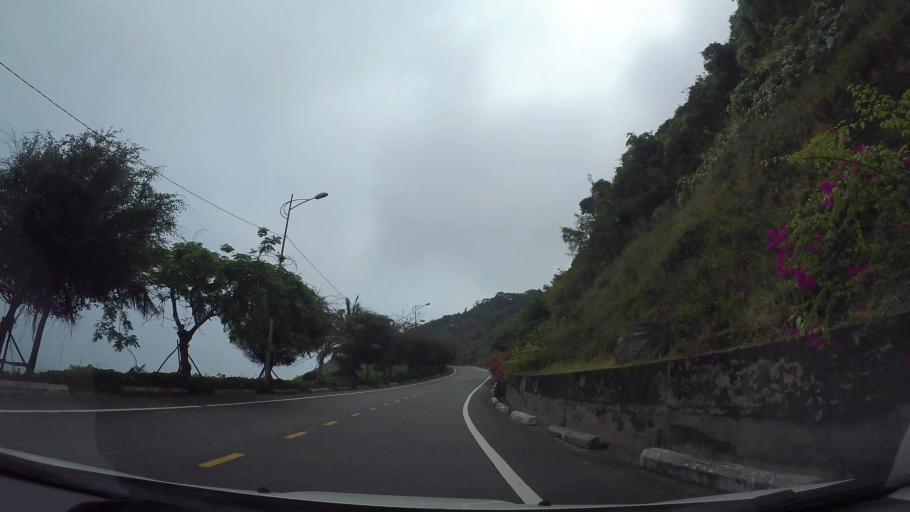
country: VN
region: Da Nang
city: Son Tra
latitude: 16.1059
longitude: 108.3078
